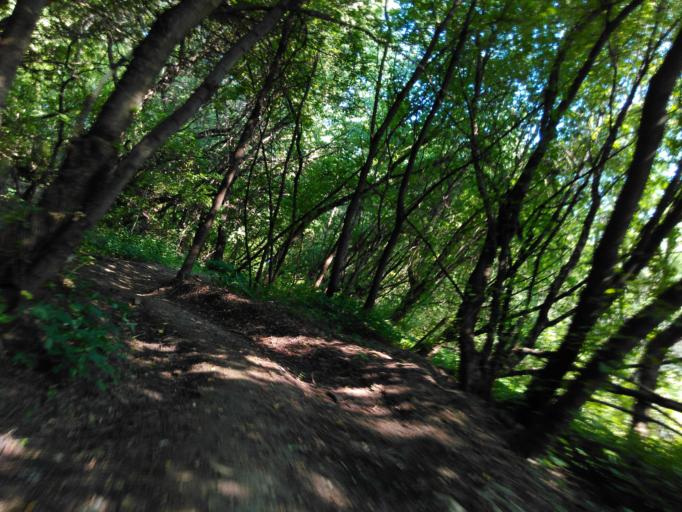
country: RU
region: Moscow
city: Amin'yevo
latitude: 55.7135
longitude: 37.4513
